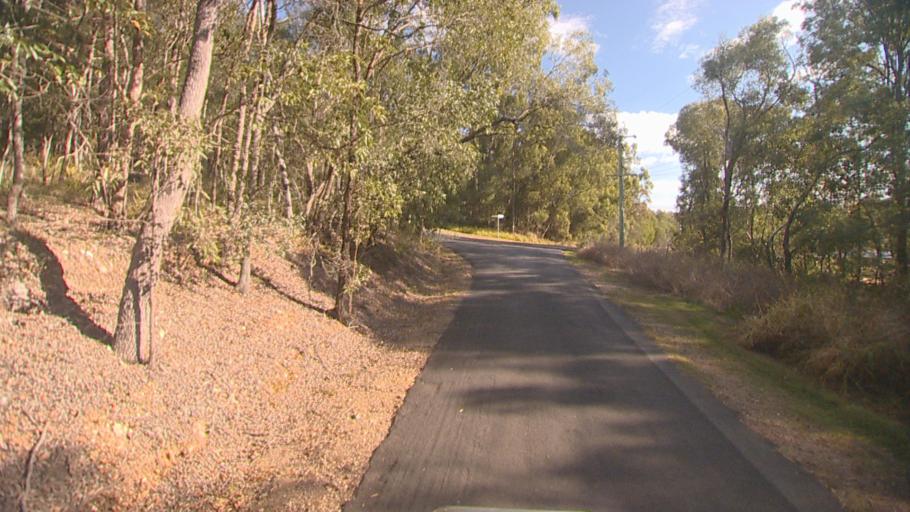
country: AU
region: Queensland
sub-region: Logan
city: Windaroo
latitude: -27.7401
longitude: 153.1657
